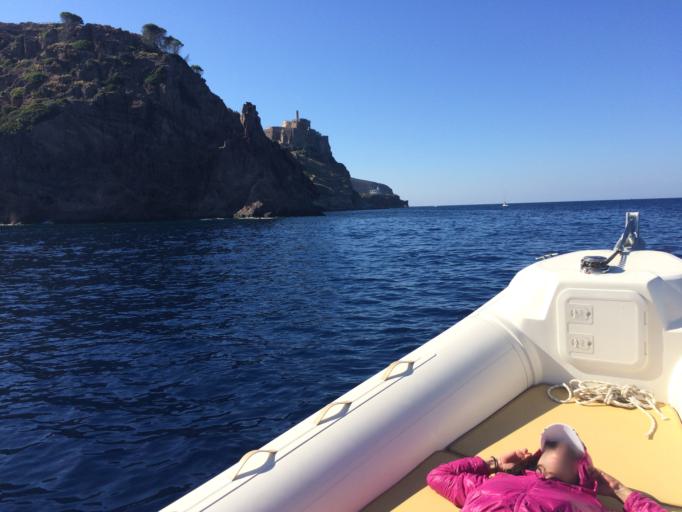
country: IT
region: Tuscany
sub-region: Provincia di Livorno
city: Capraia Isola
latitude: 43.0433
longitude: 9.8494
